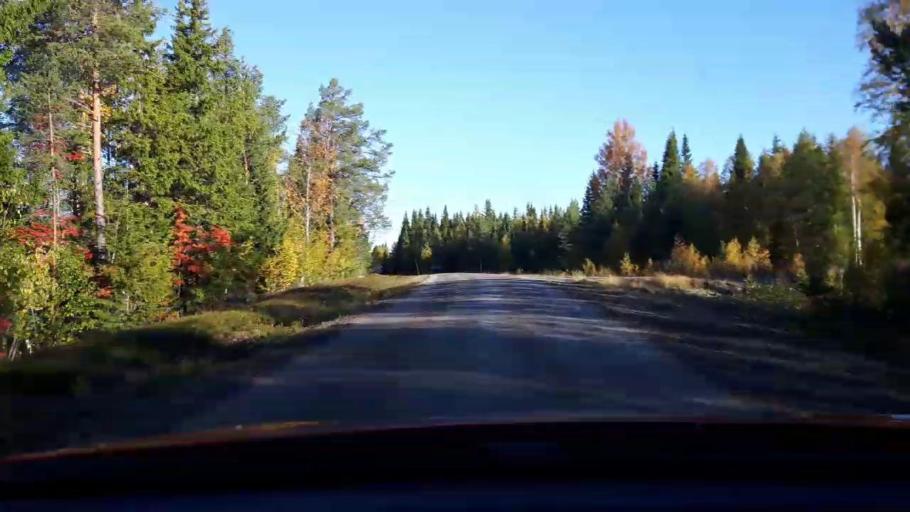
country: SE
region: Jaemtland
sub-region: Stroemsunds Kommun
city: Stroemsund
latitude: 64.3936
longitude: 15.1491
